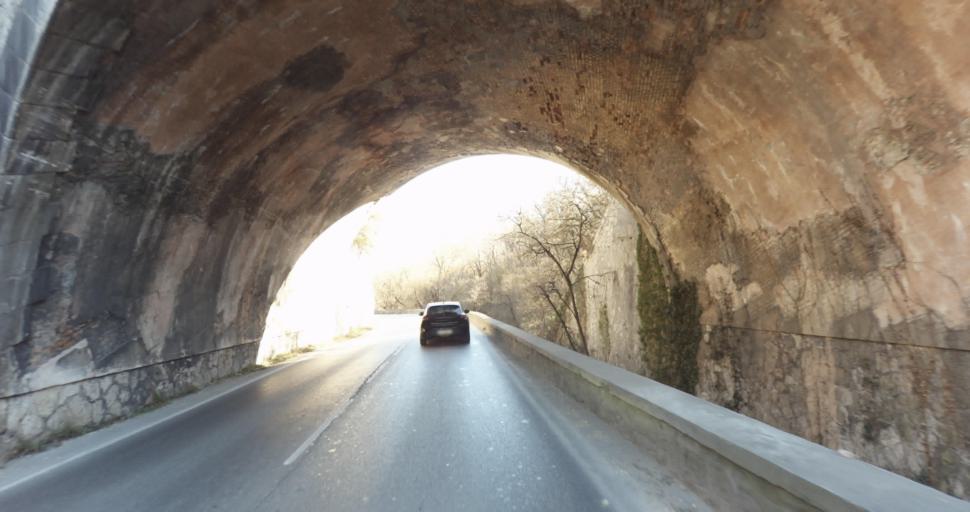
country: FR
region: Provence-Alpes-Cote d'Azur
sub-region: Departement des Bouches-du-Rhone
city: Peypin
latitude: 43.3967
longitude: 5.5751
